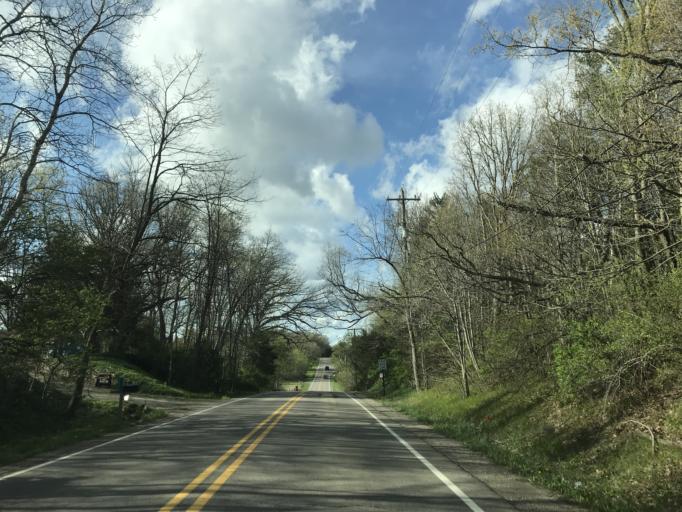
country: US
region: Michigan
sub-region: Livingston County
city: Brighton
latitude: 42.5255
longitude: -83.7204
